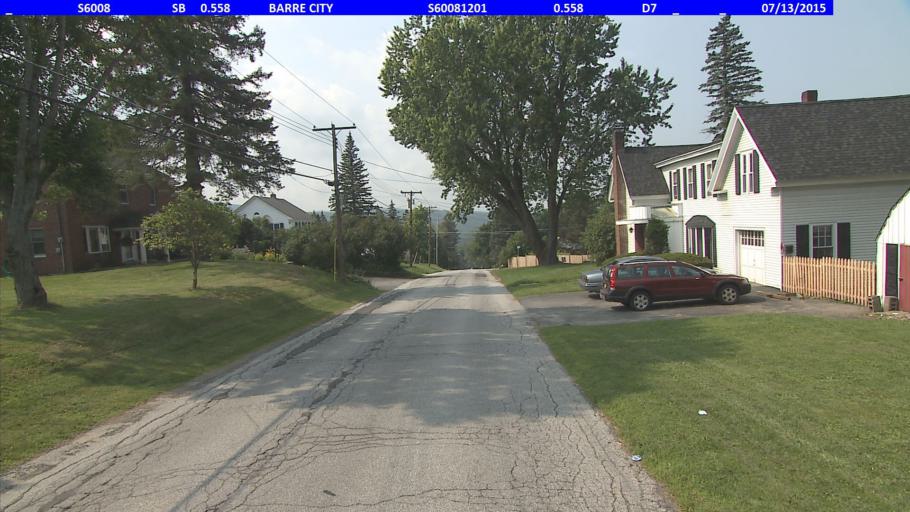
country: US
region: Vermont
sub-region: Washington County
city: Barre
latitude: 44.2003
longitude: -72.4879
